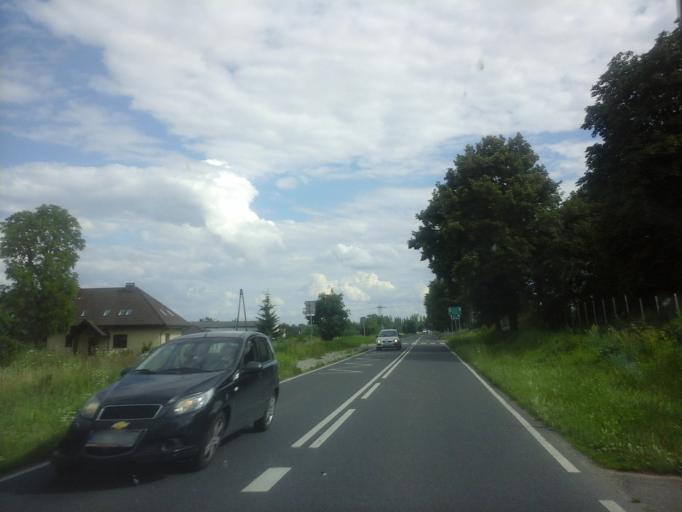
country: PL
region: West Pomeranian Voivodeship
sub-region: Powiat stargardzki
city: Stargard Szczecinski
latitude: 53.3621
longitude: 15.0061
